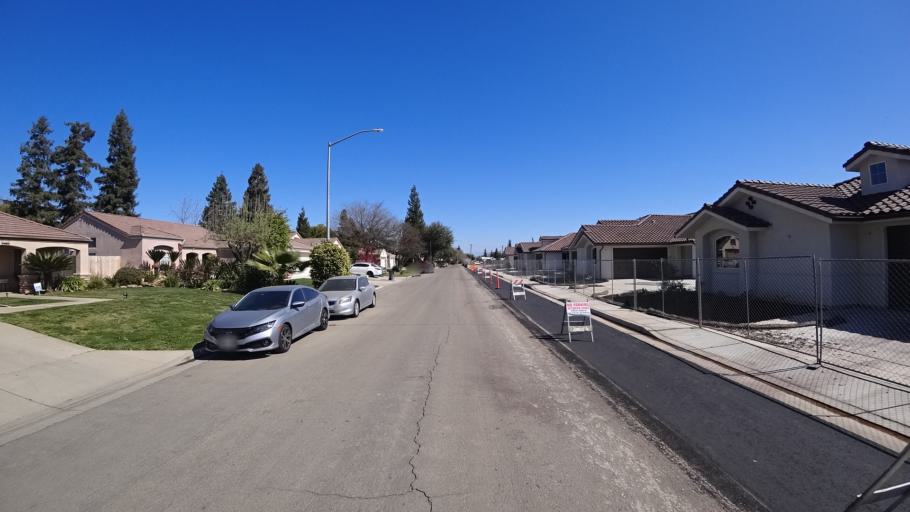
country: US
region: California
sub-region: Fresno County
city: Clovis
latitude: 36.8466
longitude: -119.7417
